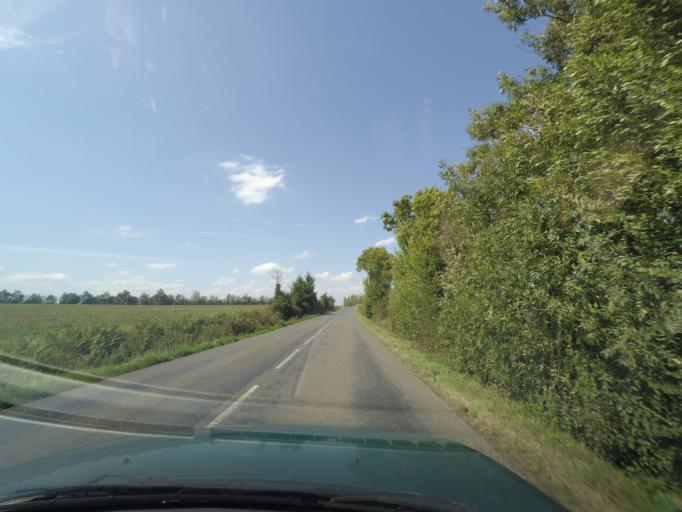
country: FR
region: Pays de la Loire
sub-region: Departement de la Loire-Atlantique
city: Saint-Lumine-de-Coutais
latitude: 47.0437
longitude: -1.7165
